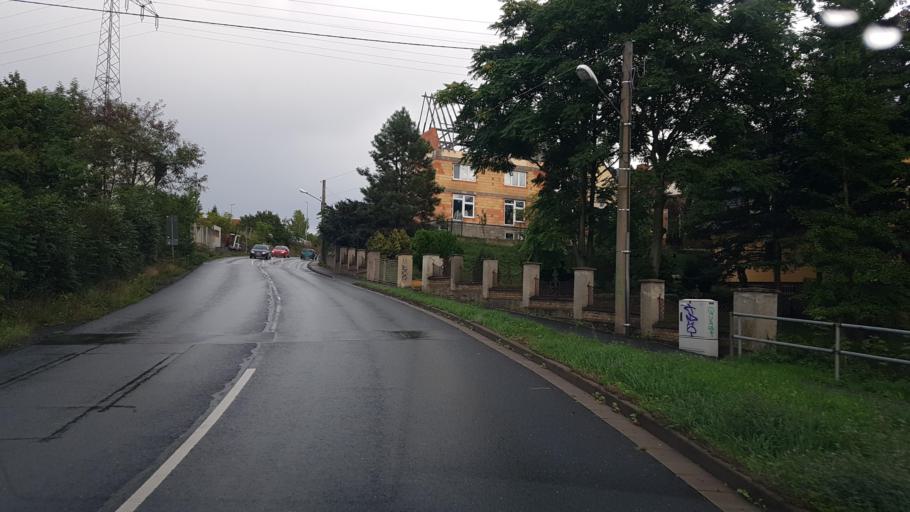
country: DE
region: Thuringia
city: Saalfeld
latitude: 50.6554
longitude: 11.3800
